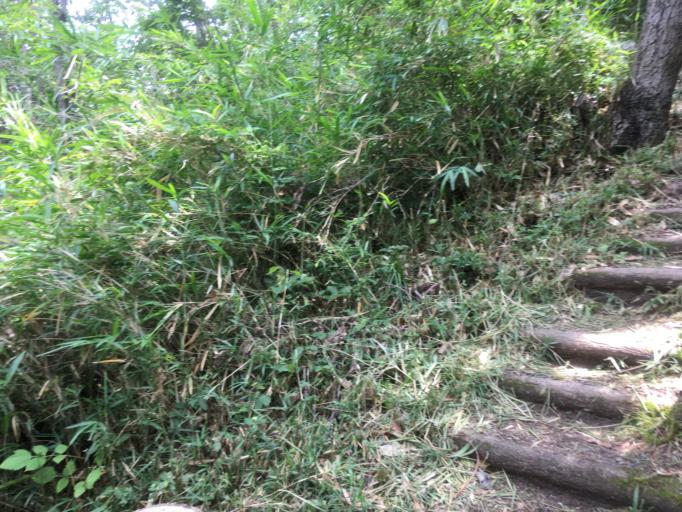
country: JP
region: Nara
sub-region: Ikoma-shi
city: Ikoma
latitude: 34.6902
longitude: 135.6621
